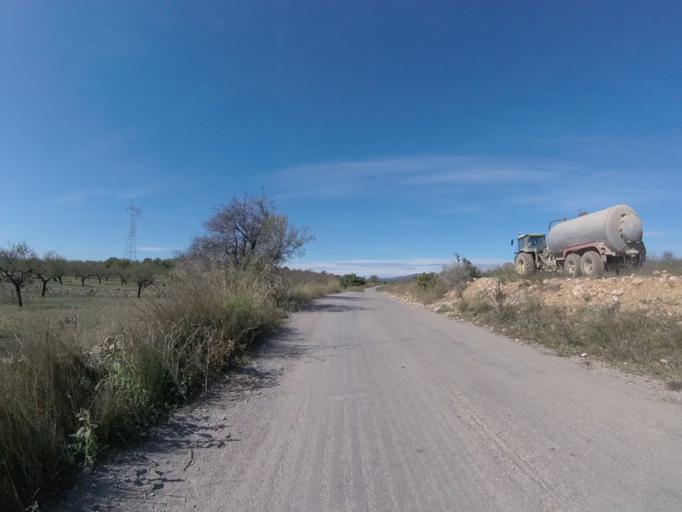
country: ES
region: Valencia
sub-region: Provincia de Castello
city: Benlloch
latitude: 40.2097
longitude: 0.0412
